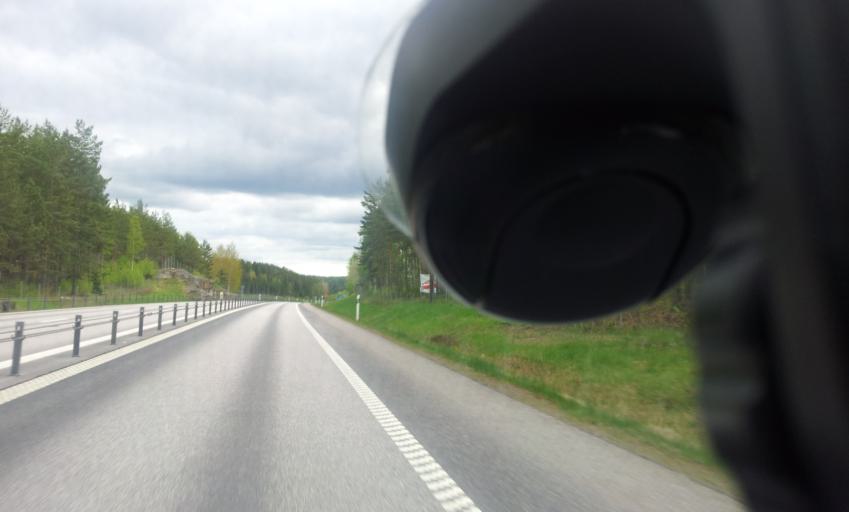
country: SE
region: OEstergoetland
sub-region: Valdemarsviks Kommun
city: Valdemarsvik
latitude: 58.2336
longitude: 16.5501
